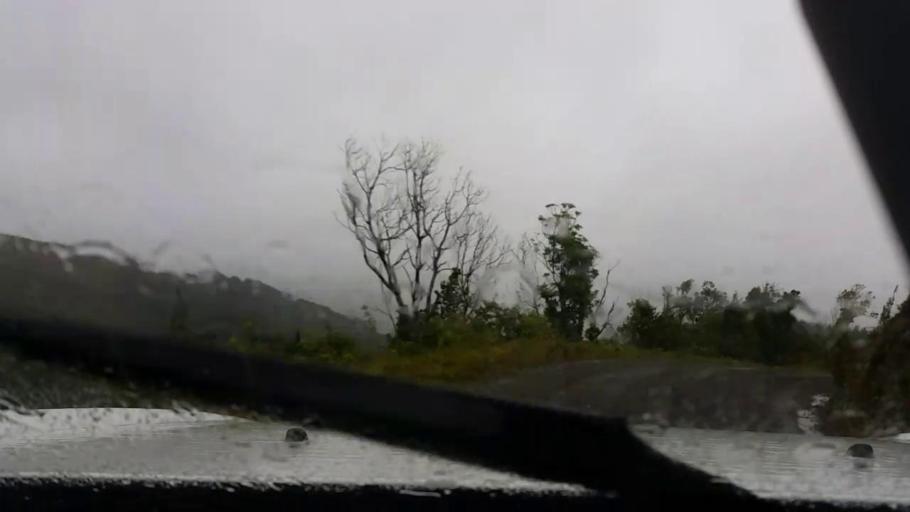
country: NZ
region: Wellington
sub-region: Masterton District
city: Masterton
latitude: -41.2042
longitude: 175.8129
